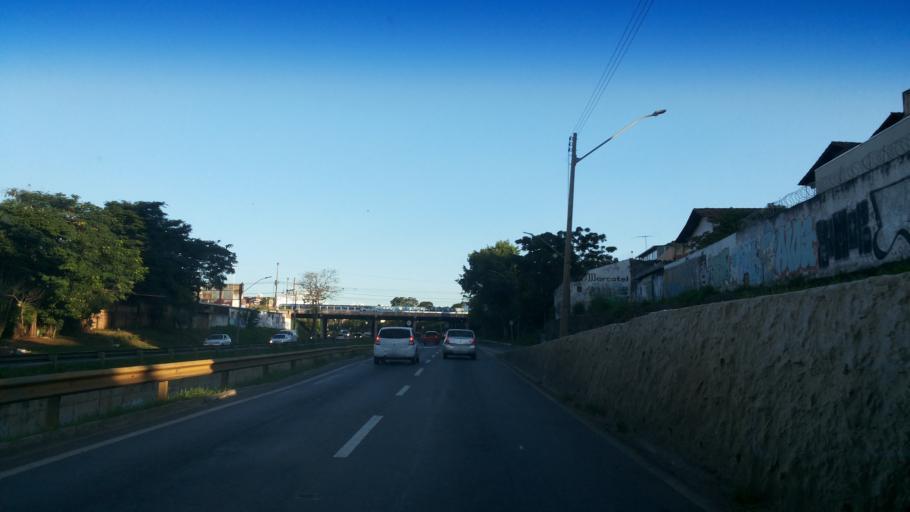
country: BR
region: Goias
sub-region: Goiania
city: Goiania
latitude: -16.6770
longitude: -49.2497
